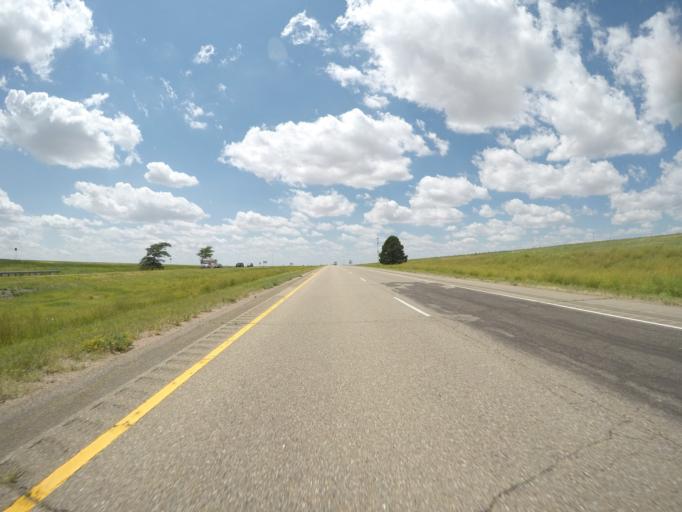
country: US
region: Colorado
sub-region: Kit Carson County
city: Burlington
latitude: 39.2941
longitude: -102.4285
